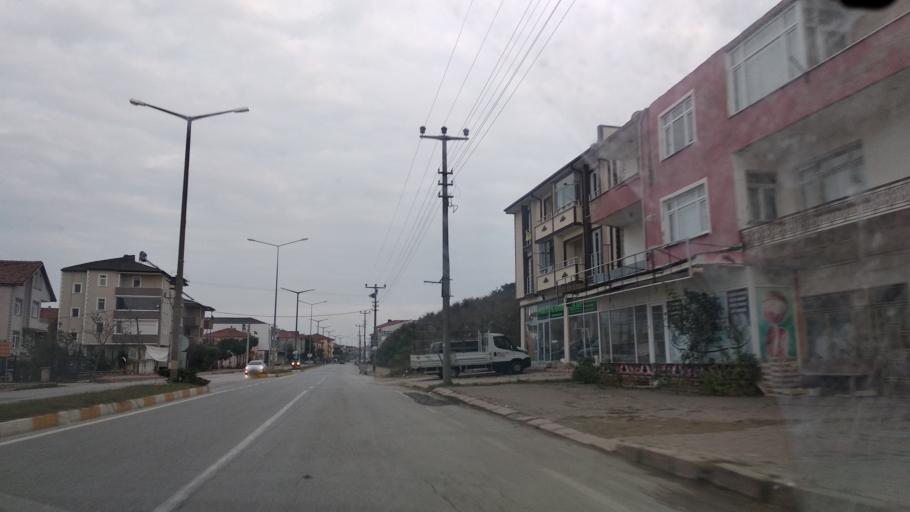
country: TR
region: Sakarya
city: Karasu
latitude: 41.0976
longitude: 30.6761
